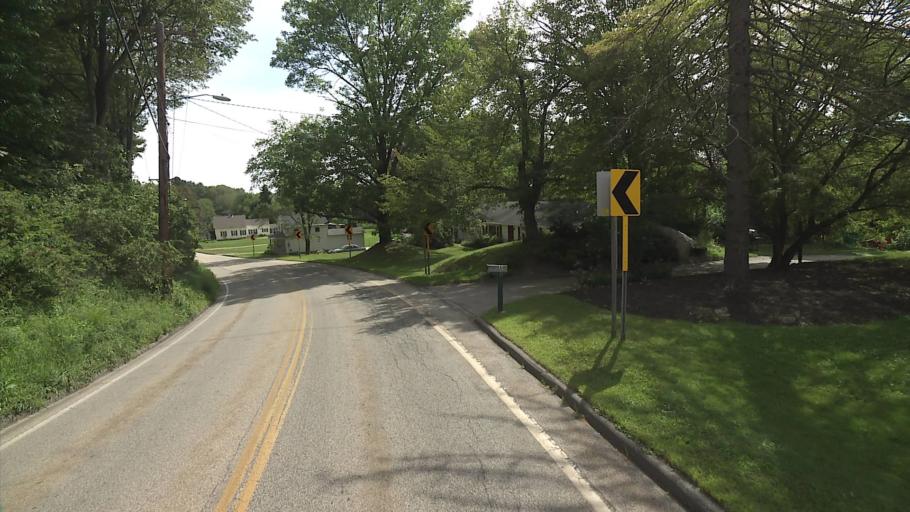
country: US
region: Connecticut
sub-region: Windham County
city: South Woodstock
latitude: 41.9370
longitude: -71.9653
